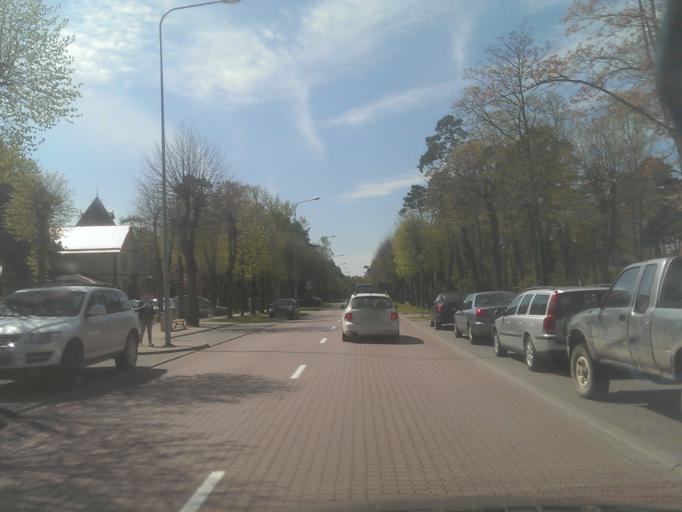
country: LV
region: Ventspils
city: Ventspils
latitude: 57.3882
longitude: 21.5438
